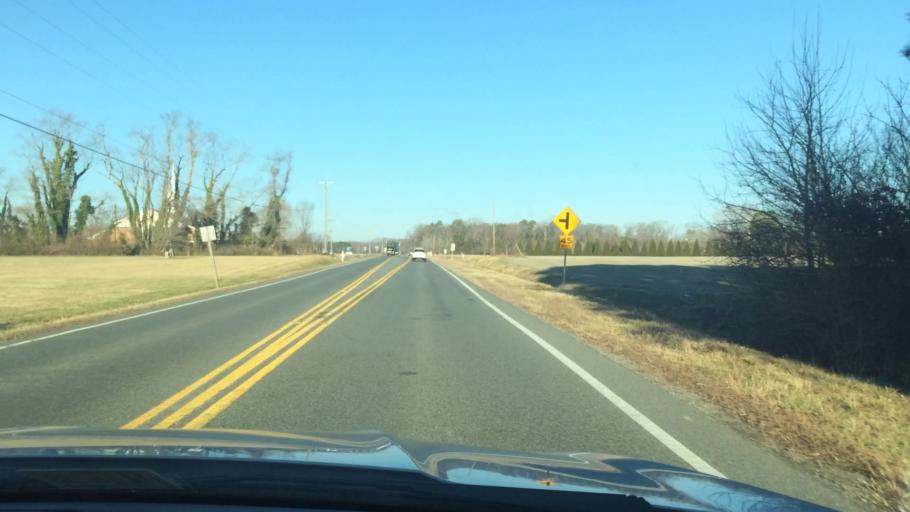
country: US
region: Virginia
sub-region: Lancaster County
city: Kilmarnock
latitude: 37.7518
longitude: -76.4103
